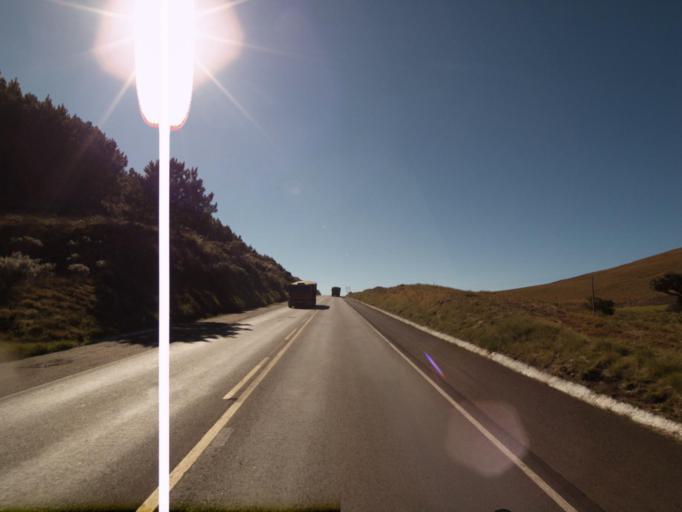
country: BR
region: Parana
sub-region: Palmas
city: Palmas
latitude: -26.6580
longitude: -51.5361
